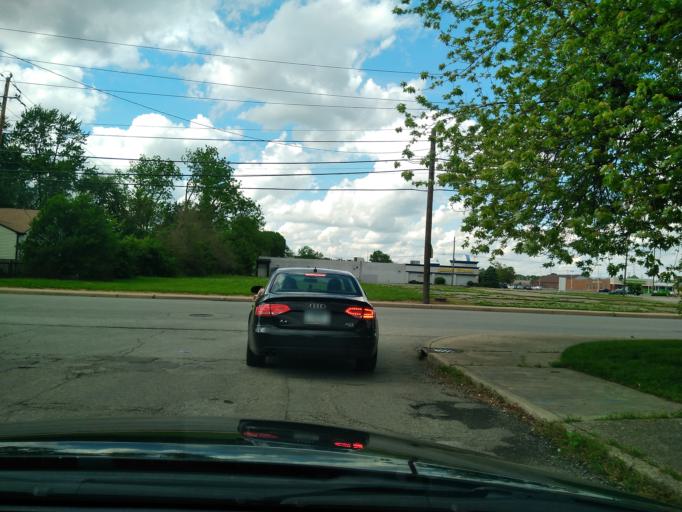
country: US
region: Indiana
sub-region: Marion County
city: Broad Ripple
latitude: 39.8475
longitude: -86.1266
